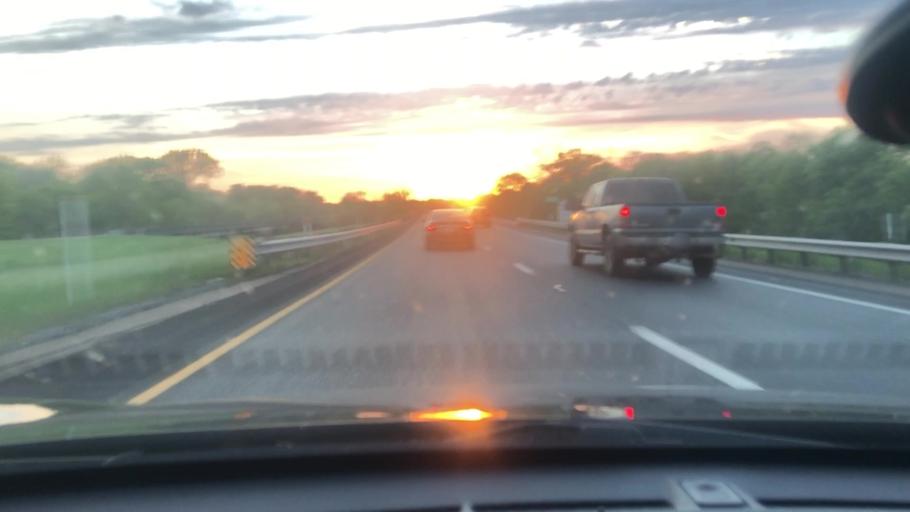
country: US
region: Texas
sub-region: Jackson County
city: Edna
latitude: 28.9602
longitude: -96.6845
